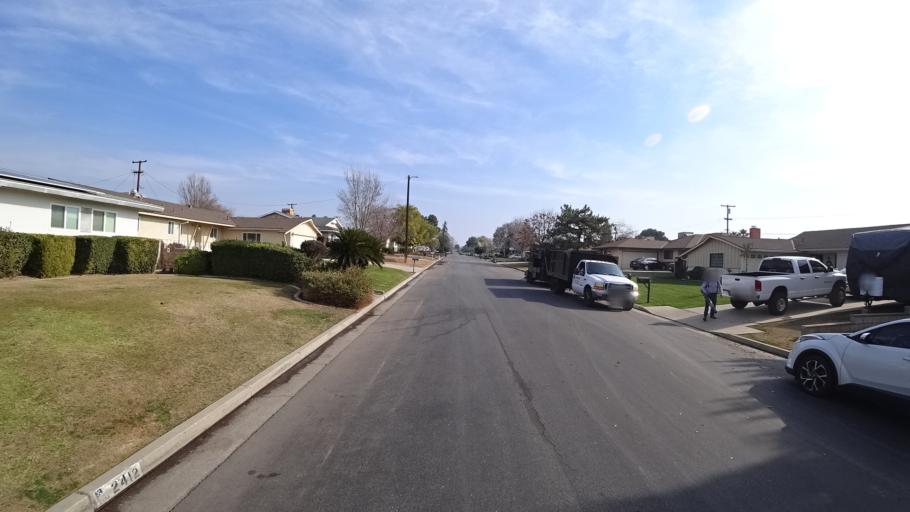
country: US
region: California
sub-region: Kern County
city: Oildale
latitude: 35.4013
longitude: -118.9658
